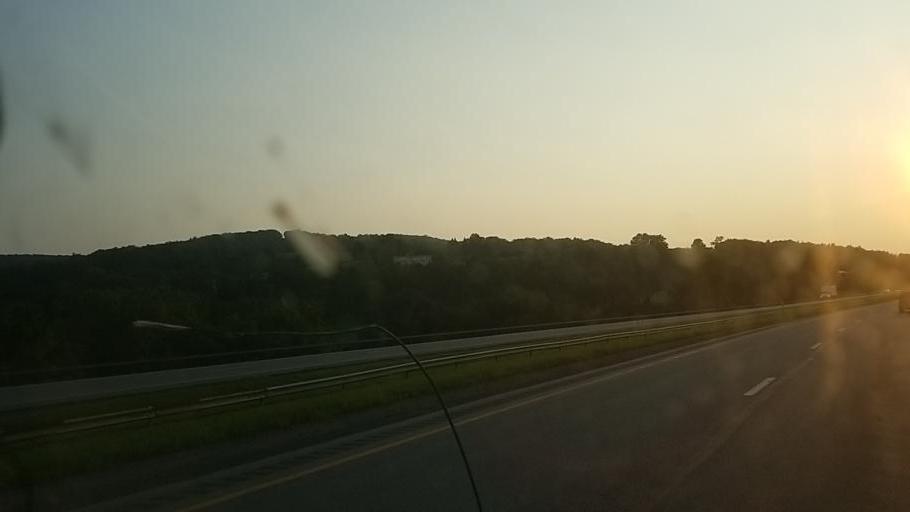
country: US
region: New York
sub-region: Herkimer County
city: Little Falls
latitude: 43.0048
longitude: -74.8856
